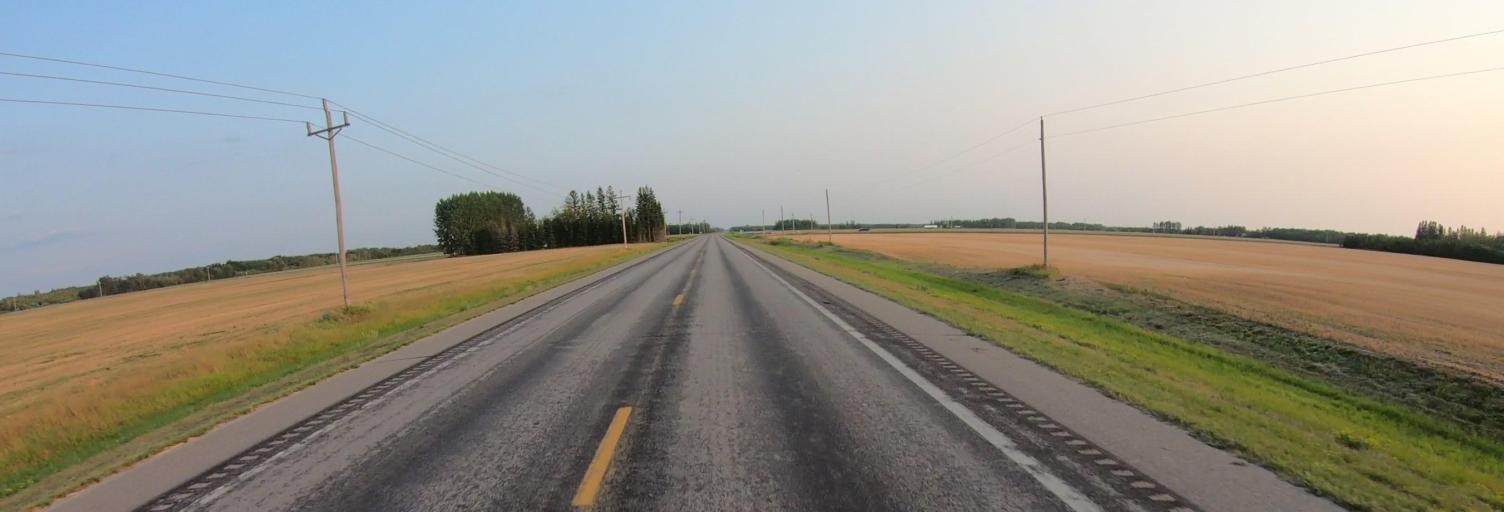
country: US
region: Minnesota
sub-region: Roseau County
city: Warroad
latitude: 48.8614
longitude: -95.3305
